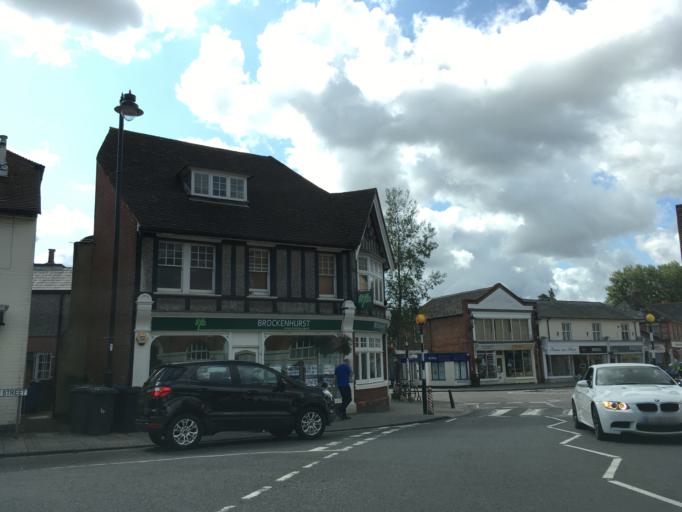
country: GB
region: England
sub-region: Hampshire
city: Overton
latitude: 51.2302
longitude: -1.3389
